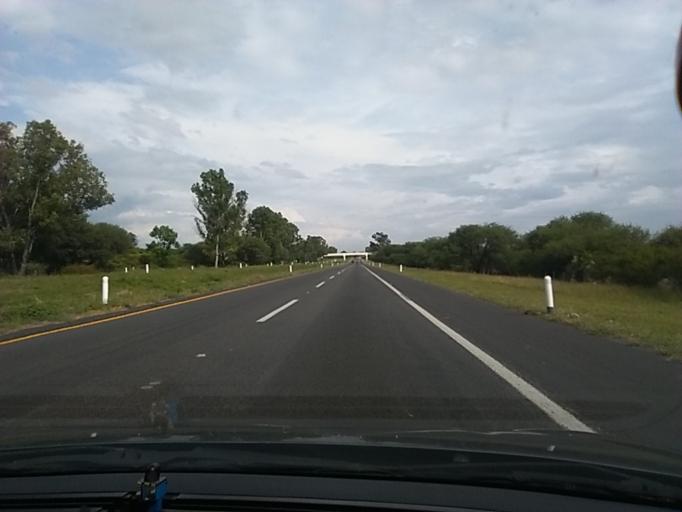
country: MX
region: Jalisco
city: La Barca
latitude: 20.3374
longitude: -102.6007
